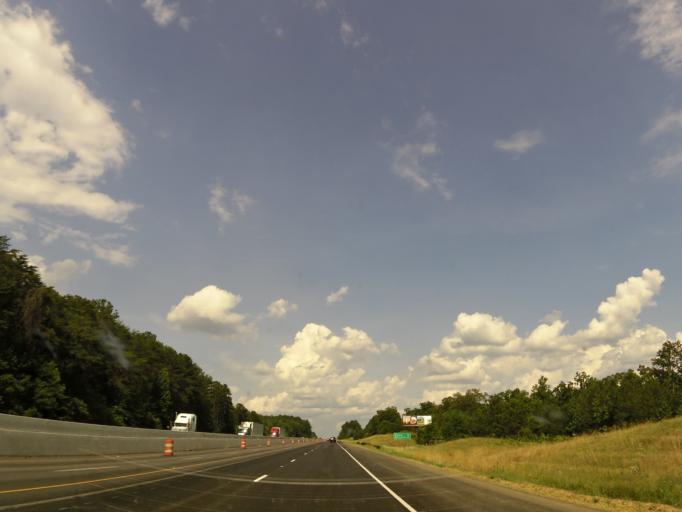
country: US
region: Alabama
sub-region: Tuscaloosa County
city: Coaling
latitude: 33.1758
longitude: -87.3966
